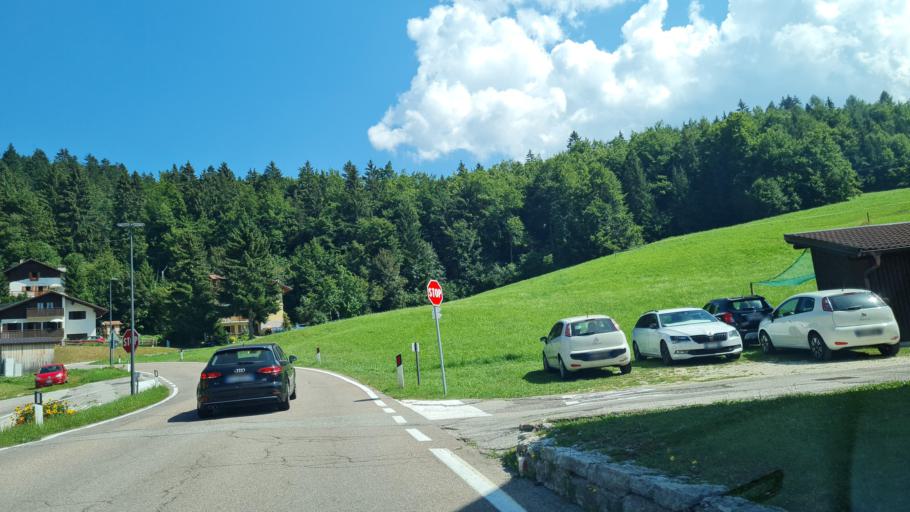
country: IT
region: Trentino-Alto Adige
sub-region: Provincia di Trento
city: Centa San Nicolo
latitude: 45.9460
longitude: 11.2396
